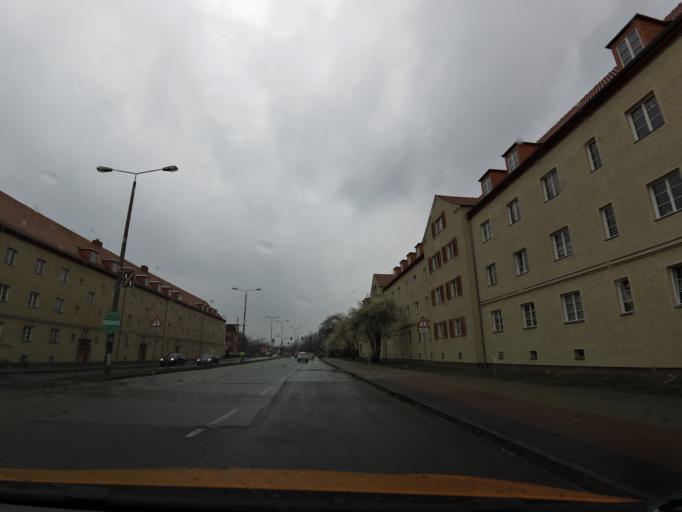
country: DE
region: Brandenburg
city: Brandenburg an der Havel
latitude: 52.3988
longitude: 12.5507
